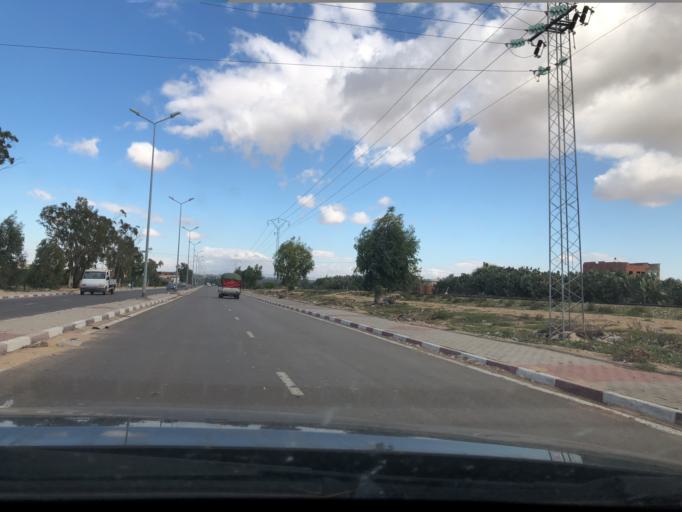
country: TN
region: Al Qasrayn
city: Kasserine
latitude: 35.1861
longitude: 8.8652
